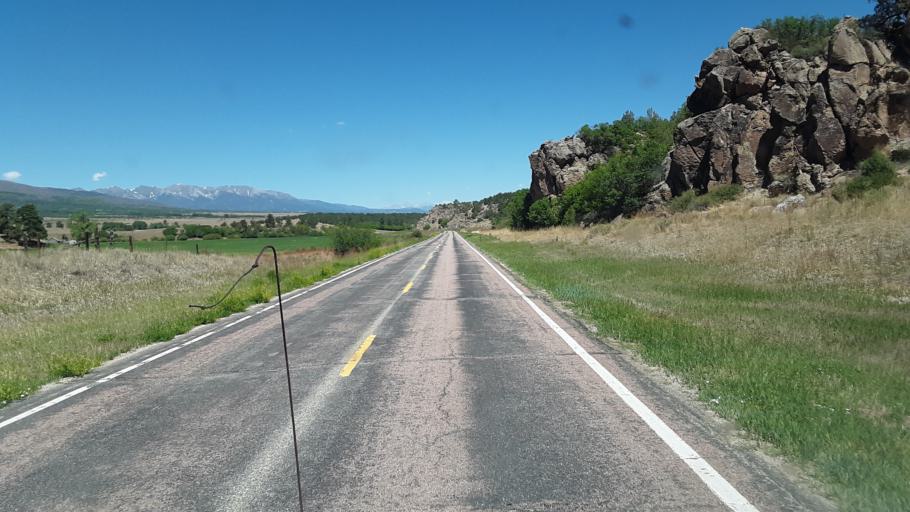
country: US
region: Colorado
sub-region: Custer County
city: Westcliffe
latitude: 38.2588
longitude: -105.5931
